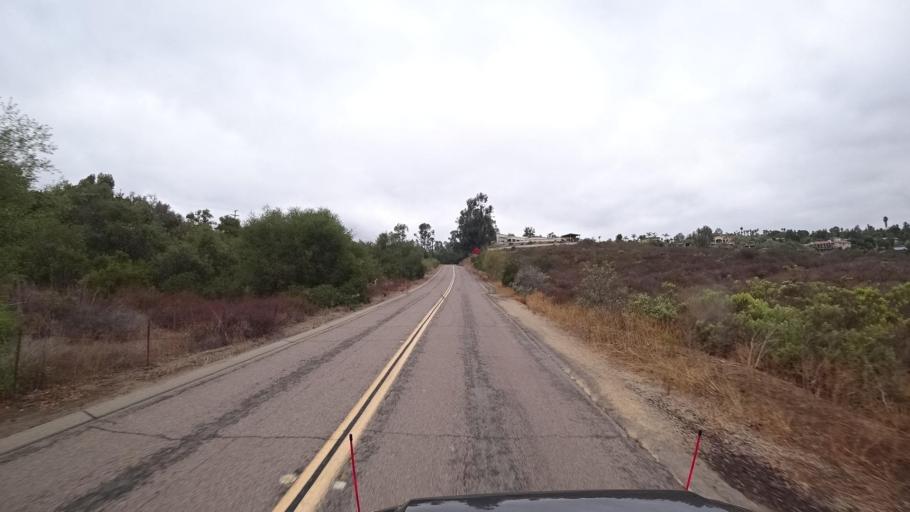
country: US
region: California
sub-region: San Diego County
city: Escondido
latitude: 33.0864
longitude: -117.1143
